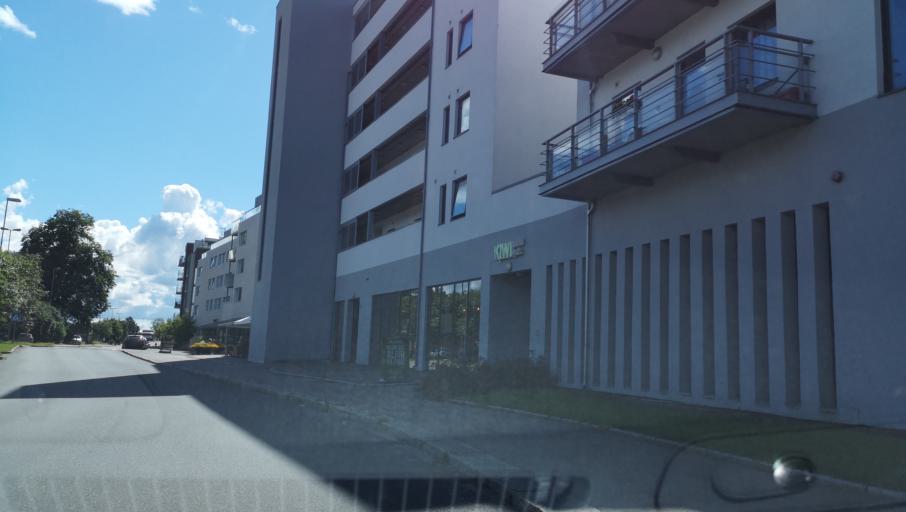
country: NO
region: Akershus
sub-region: As
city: As
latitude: 59.6642
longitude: 10.7935
